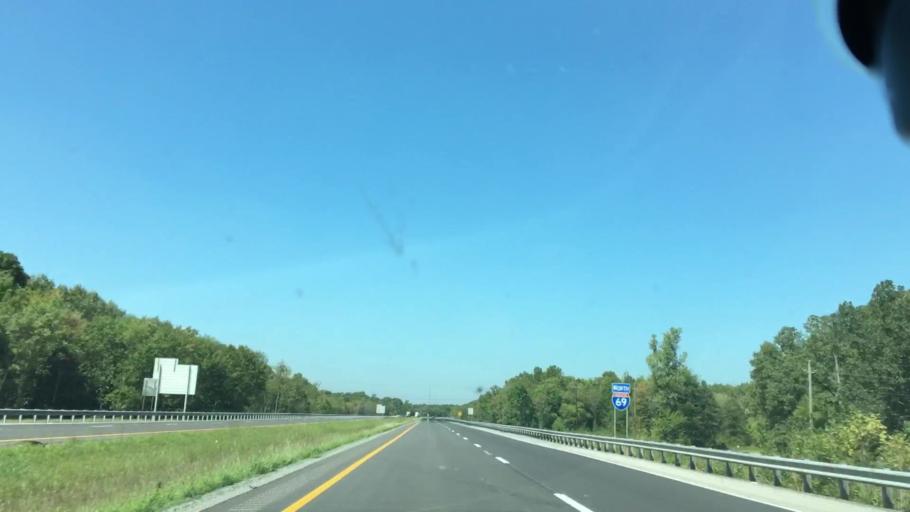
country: US
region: Kentucky
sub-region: Webster County
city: Sebree
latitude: 37.6174
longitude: -87.5018
